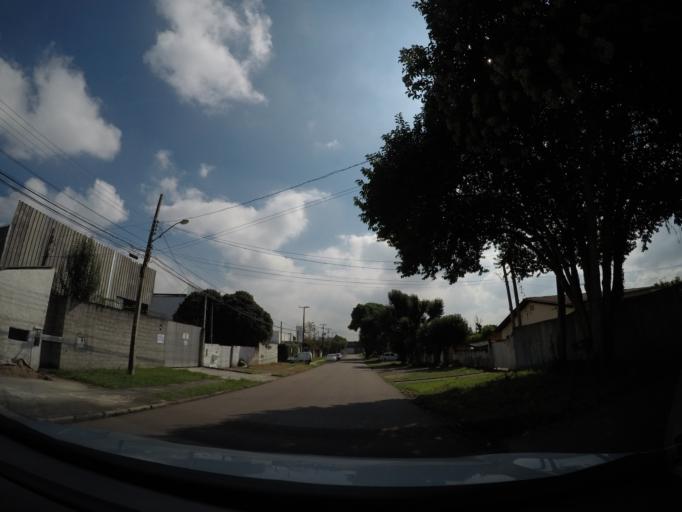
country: BR
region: Parana
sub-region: Sao Jose Dos Pinhais
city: Sao Jose dos Pinhais
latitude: -25.4997
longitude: -49.2242
